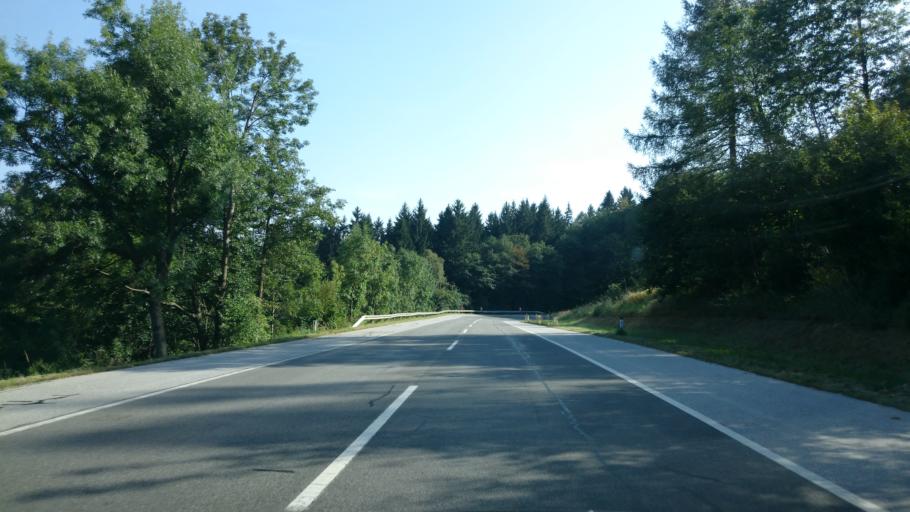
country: AT
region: Lower Austria
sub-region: Politischer Bezirk Neunkirchen
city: Monichkirchen
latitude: 47.5184
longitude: 16.0599
